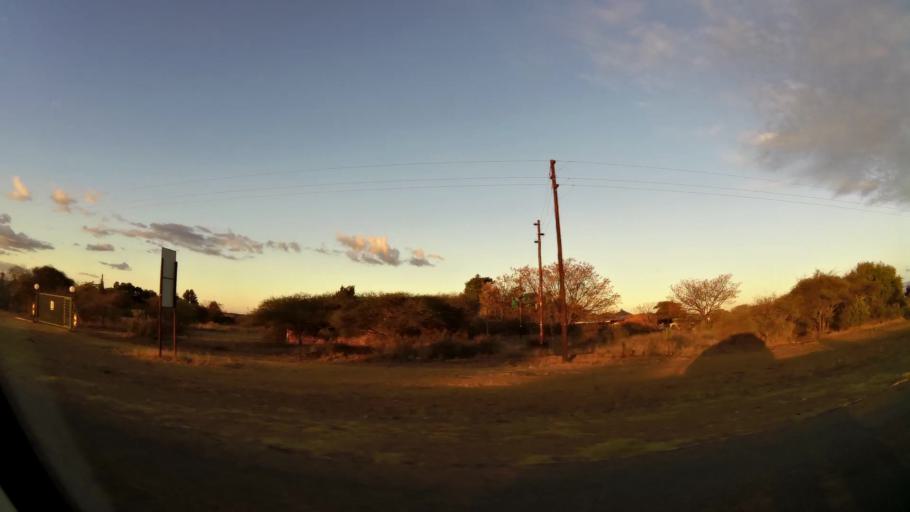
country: ZA
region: Limpopo
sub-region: Capricorn District Municipality
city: Polokwane
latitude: -23.7961
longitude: 29.4773
